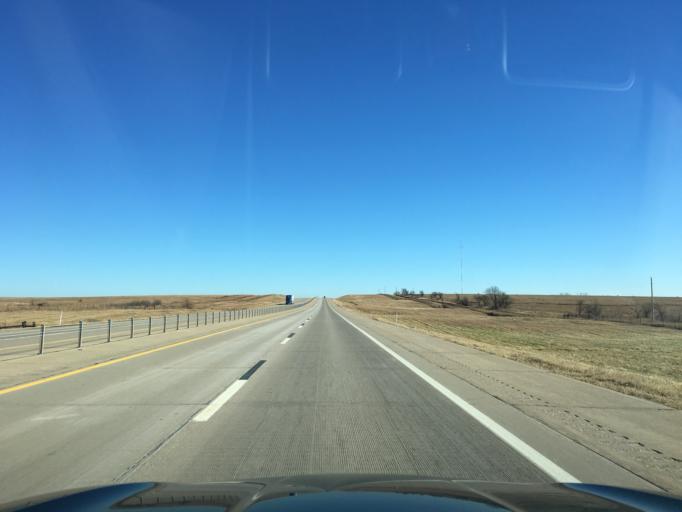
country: US
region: Oklahoma
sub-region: Noble County
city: Perry
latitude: 36.3920
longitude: -97.1587
